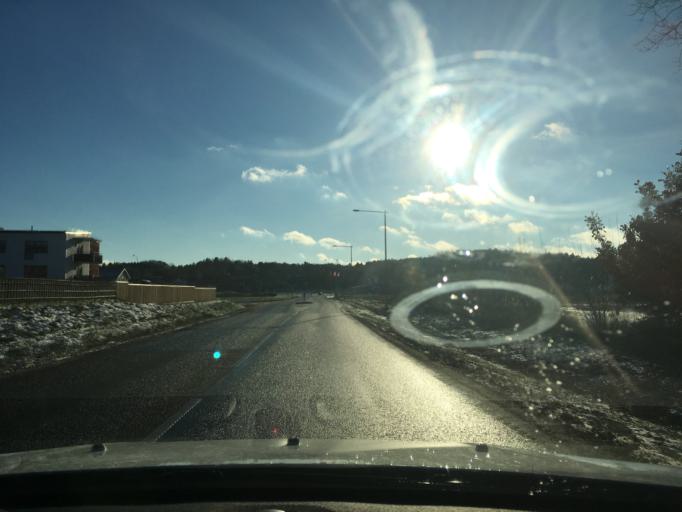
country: SE
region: Vaestra Goetaland
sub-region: Tjorns Kommun
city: Myggenas
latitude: 58.0267
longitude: 11.6564
